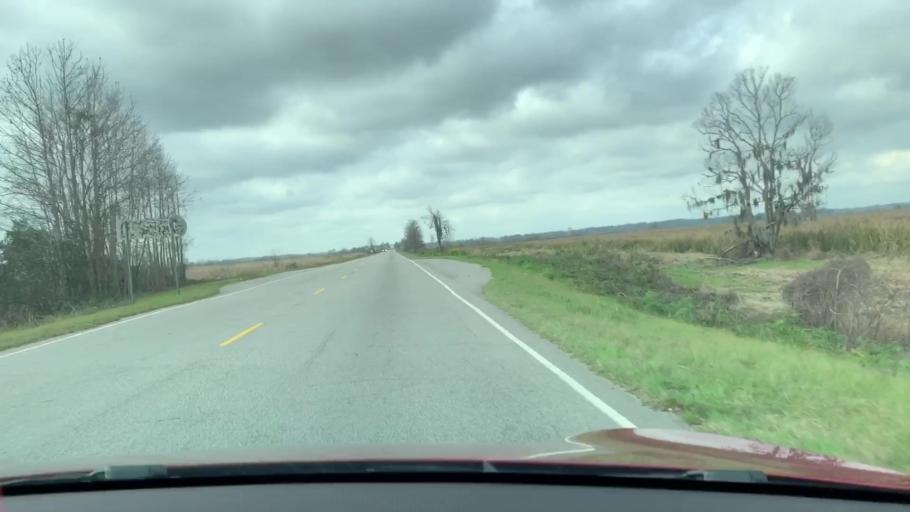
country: US
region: Georgia
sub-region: Chatham County
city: Port Wentworth
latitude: 32.1661
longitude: -81.1206
